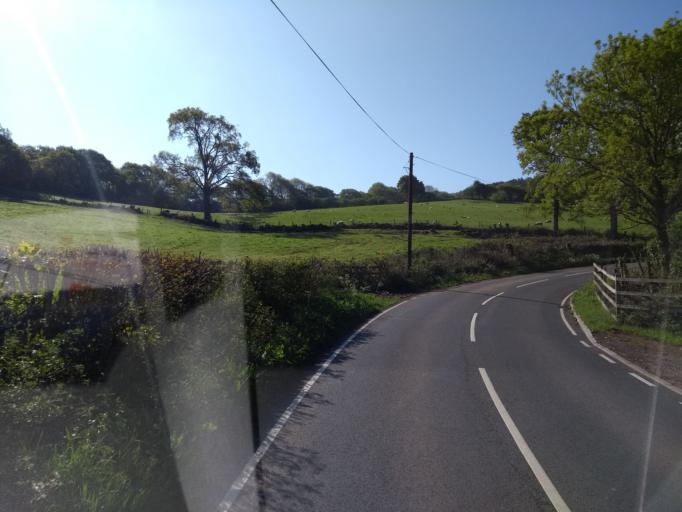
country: GB
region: England
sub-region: Somerset
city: Taunton
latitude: 50.9509
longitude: -3.0854
